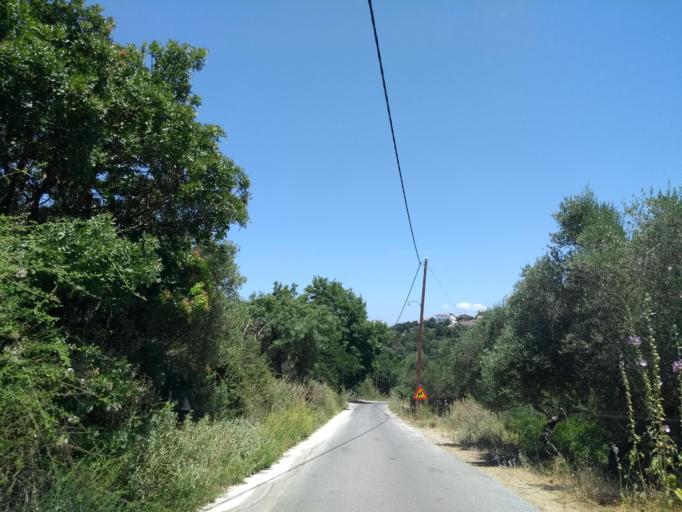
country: GR
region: Crete
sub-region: Nomos Chanias
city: Georgioupolis
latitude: 35.3172
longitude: 24.3039
